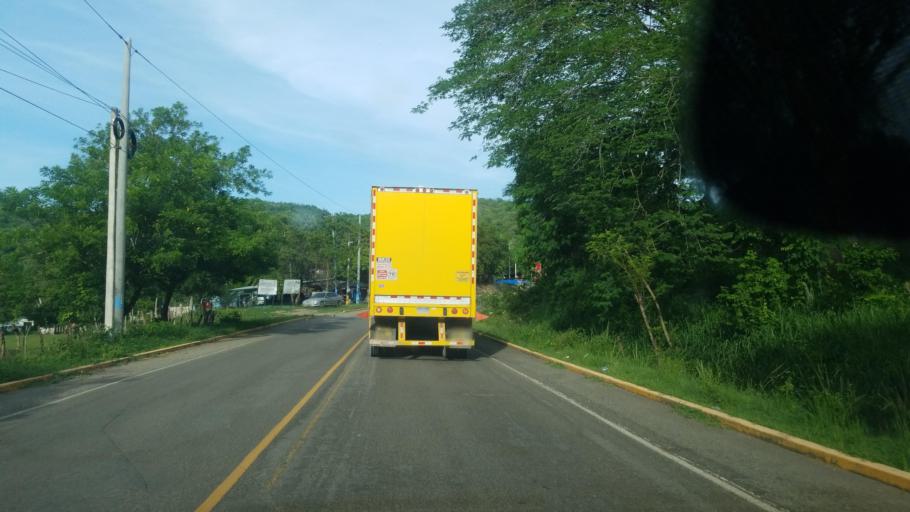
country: HN
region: Santa Barbara
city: Ilama
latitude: 15.0662
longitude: -88.2273
